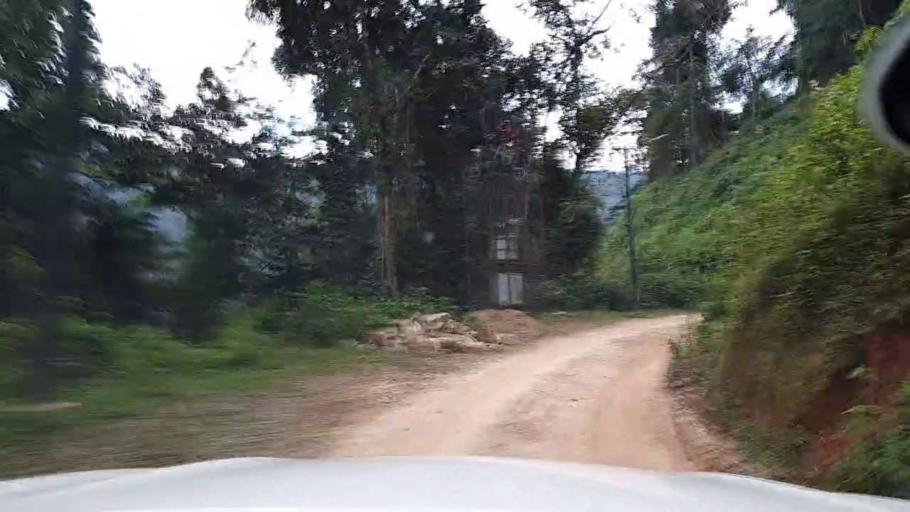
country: RW
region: Western Province
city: Cyangugu
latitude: -2.5609
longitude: 29.2283
